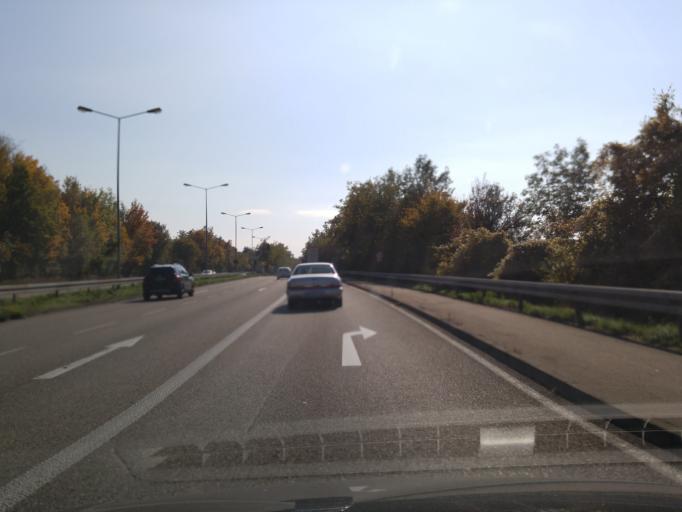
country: DE
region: Baden-Wuerttemberg
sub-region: Regierungsbezirk Stuttgart
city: Neckarsulm
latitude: 49.1695
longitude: 9.2250
